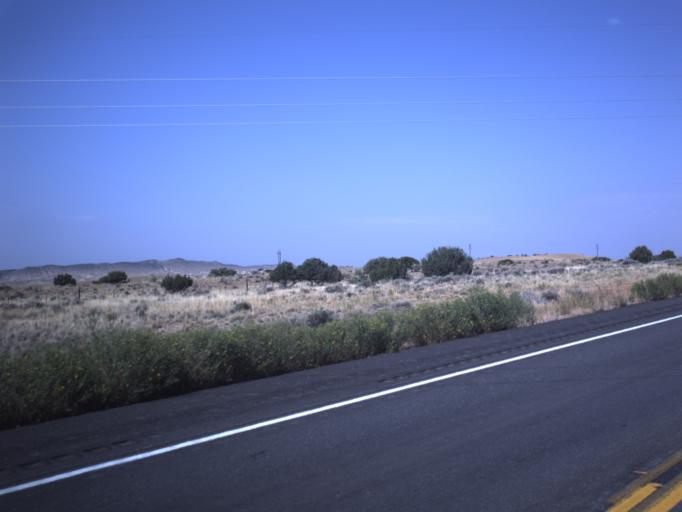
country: US
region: Utah
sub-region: Uintah County
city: Naples
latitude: 40.3218
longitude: -109.2592
